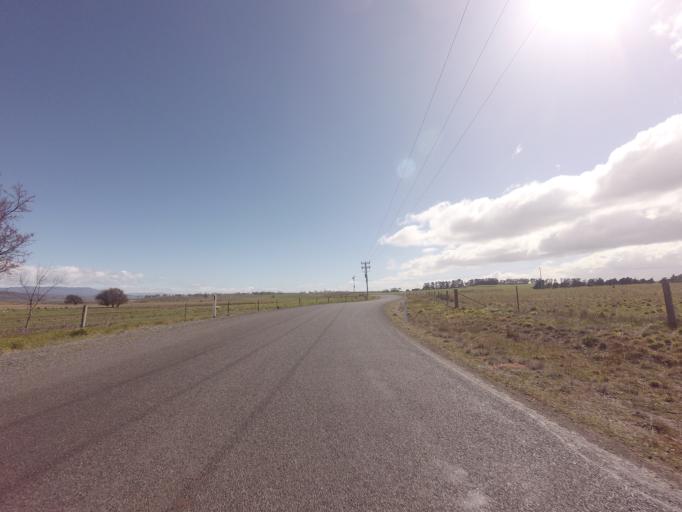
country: AU
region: Tasmania
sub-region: Northern Midlands
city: Evandale
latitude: -41.9215
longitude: 147.4822
